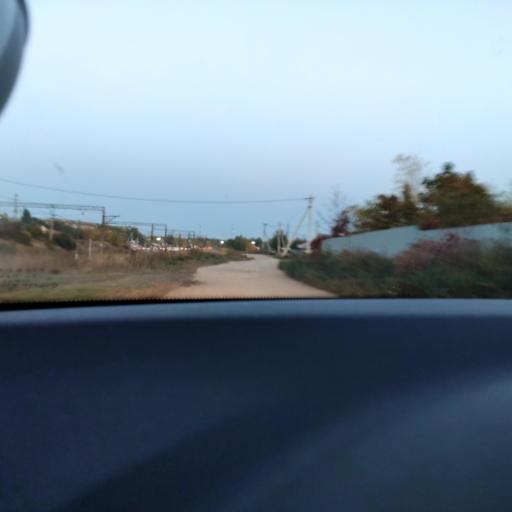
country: RU
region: Samara
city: Novosemeykino
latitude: 53.3694
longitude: 50.3491
